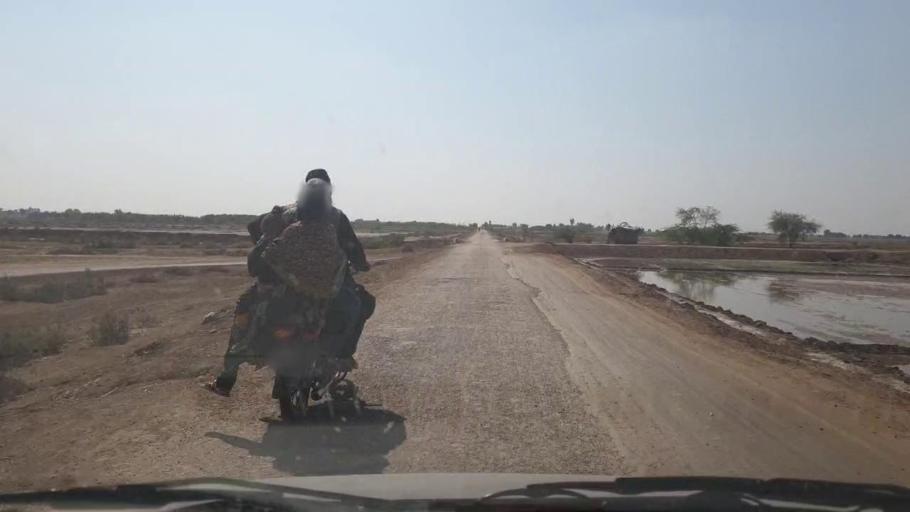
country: PK
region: Sindh
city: Samaro
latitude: 25.2381
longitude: 69.3401
